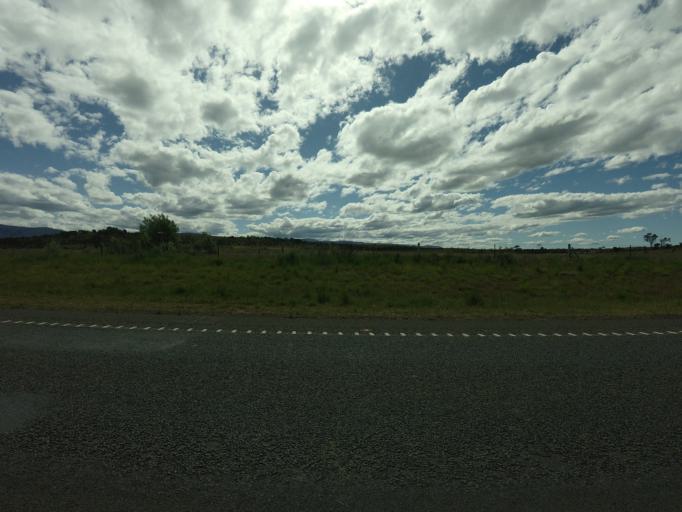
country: AU
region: Tasmania
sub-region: Northern Midlands
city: Evandale
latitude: -42.1366
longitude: 147.4230
